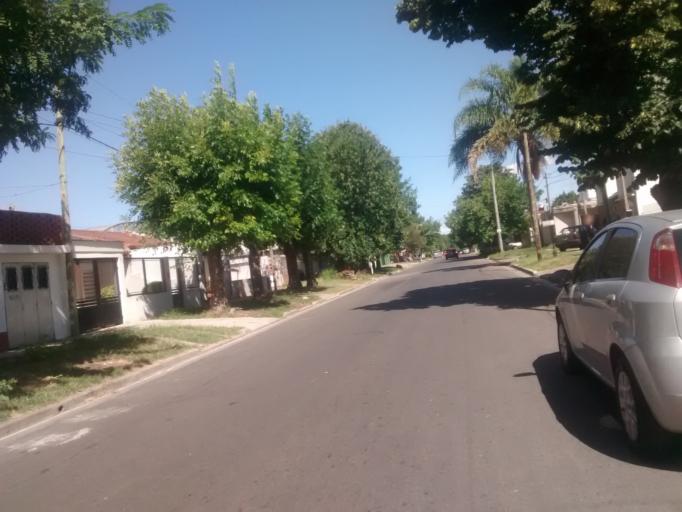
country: AR
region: Buenos Aires
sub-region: Partido de La Plata
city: La Plata
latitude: -34.9357
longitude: -57.9241
